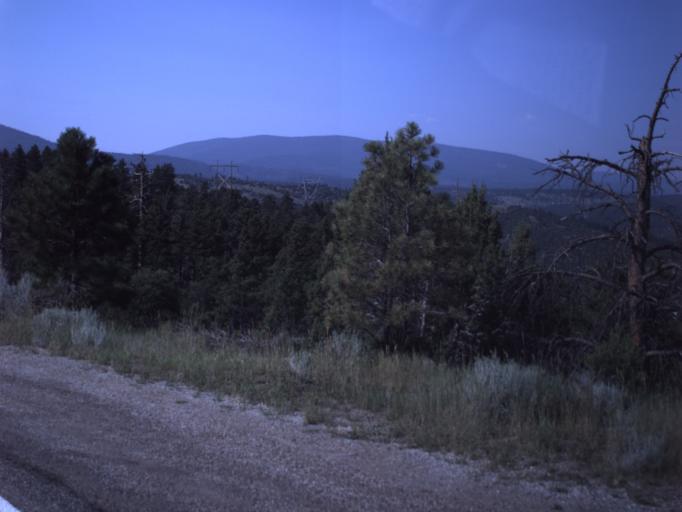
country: US
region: Utah
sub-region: Daggett County
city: Manila
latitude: 40.9180
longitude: -109.4150
